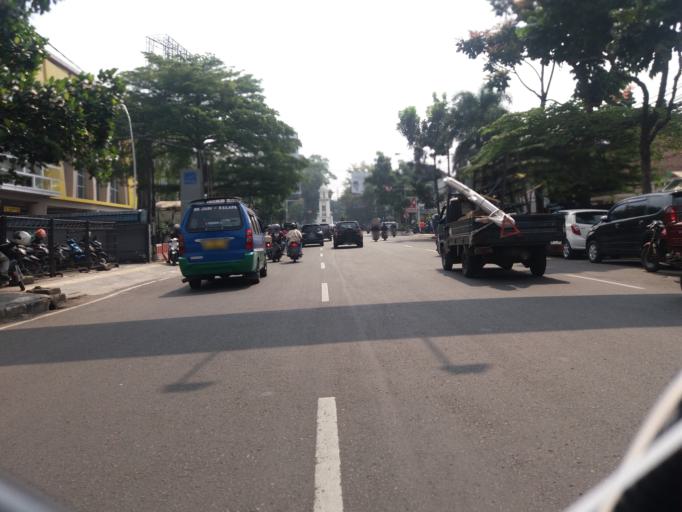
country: ID
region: West Java
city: Bandung
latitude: -6.9053
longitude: 107.6044
